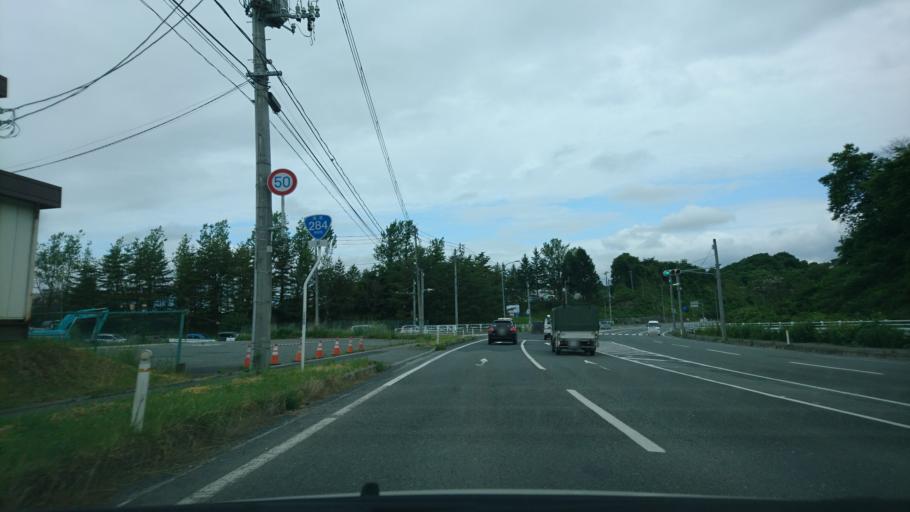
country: JP
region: Iwate
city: Ichinoseki
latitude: 38.9088
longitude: 141.1474
